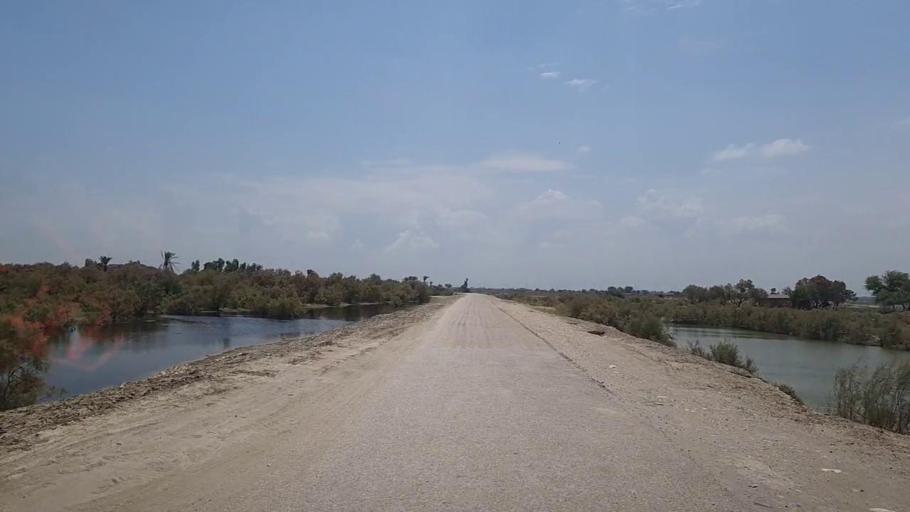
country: PK
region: Sindh
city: Kandhkot
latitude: 28.2826
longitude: 69.1693
